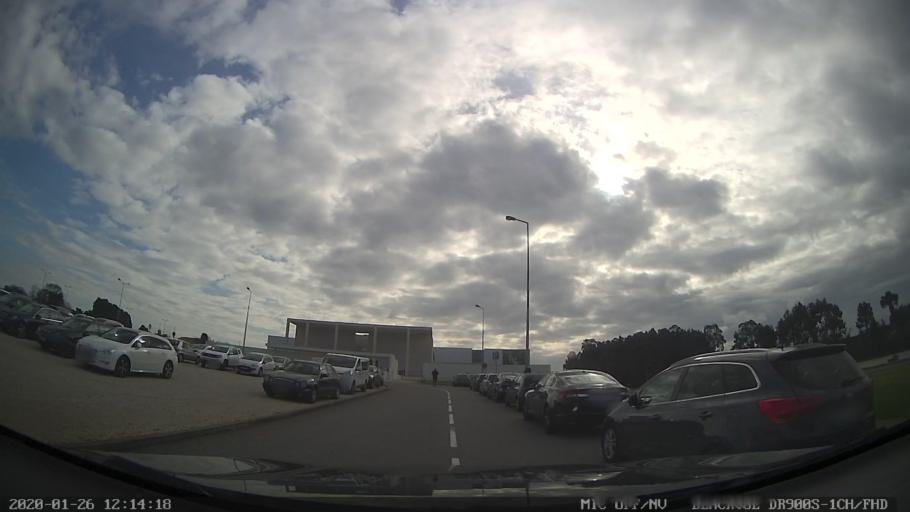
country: PT
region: Aveiro
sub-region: Aveiro
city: Aveiro
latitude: 40.6352
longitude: -8.6334
